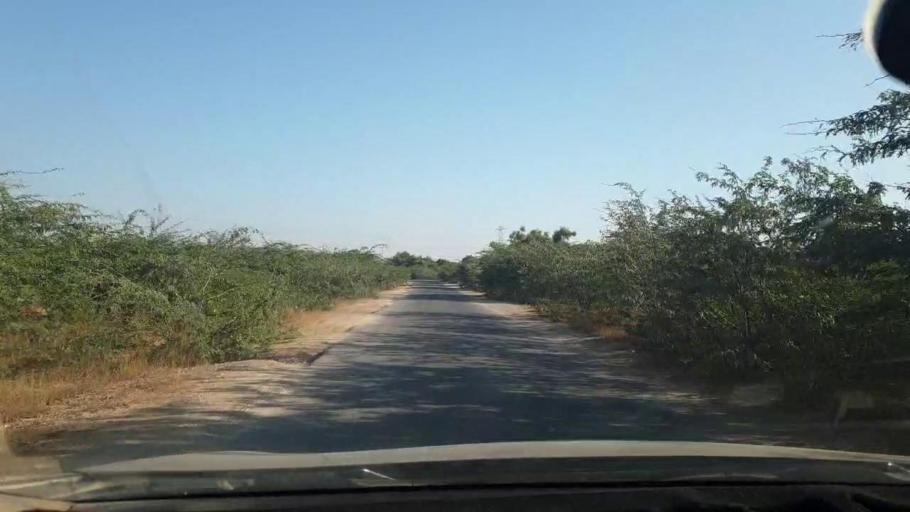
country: PK
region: Sindh
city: Malir Cantonment
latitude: 25.1561
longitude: 67.1918
